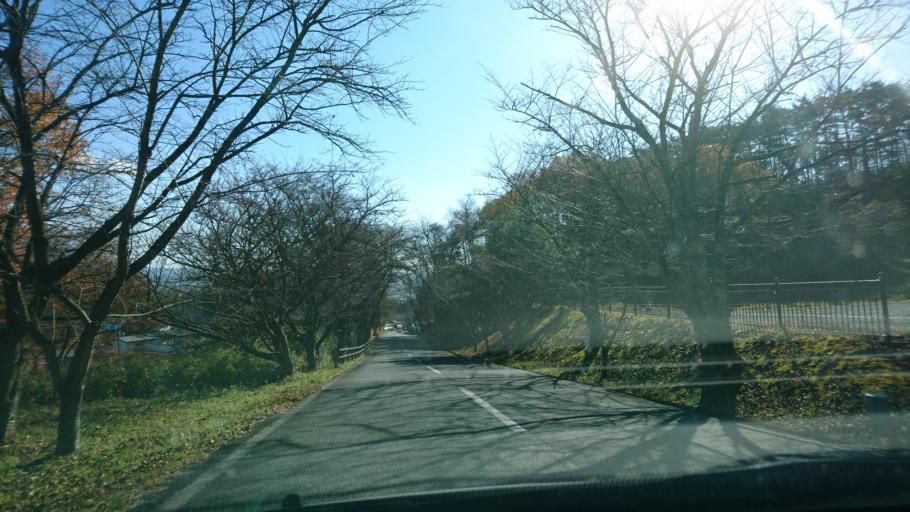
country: JP
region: Iwate
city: Ichinoseki
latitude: 38.9934
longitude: 141.1061
